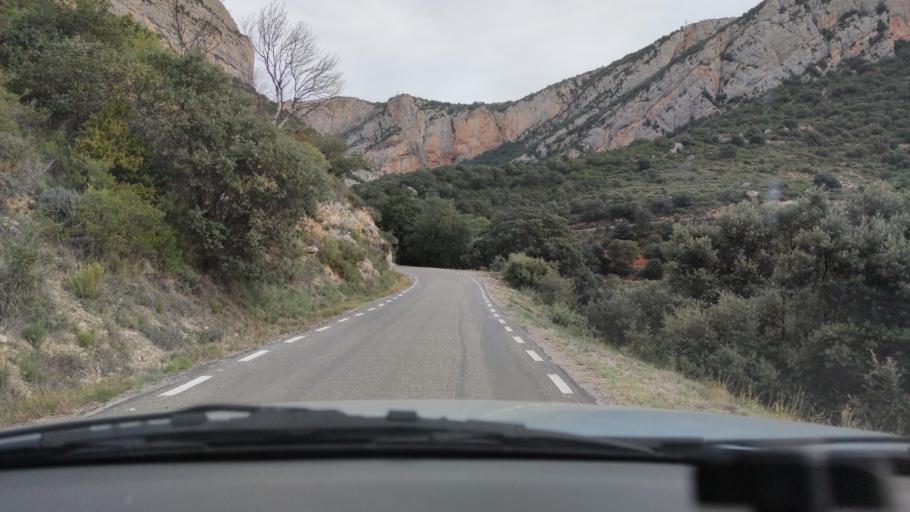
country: ES
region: Catalonia
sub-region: Provincia de Lleida
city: Artesa de Segre
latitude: 42.0183
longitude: 1.0291
